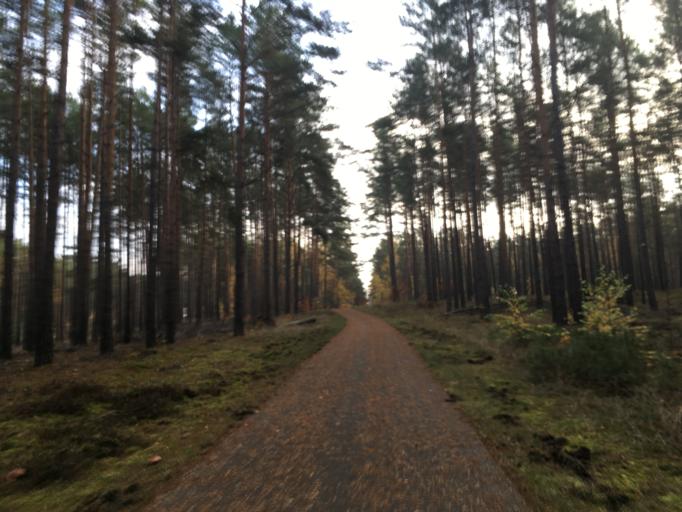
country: DE
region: Brandenburg
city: Schlepzig
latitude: 52.0322
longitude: 13.8131
